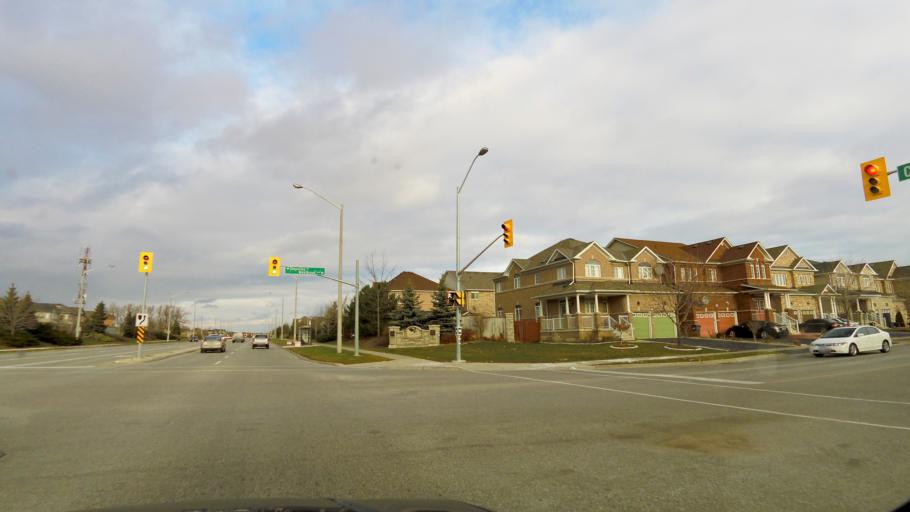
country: CA
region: Ontario
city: Brampton
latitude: 43.7766
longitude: -79.6774
